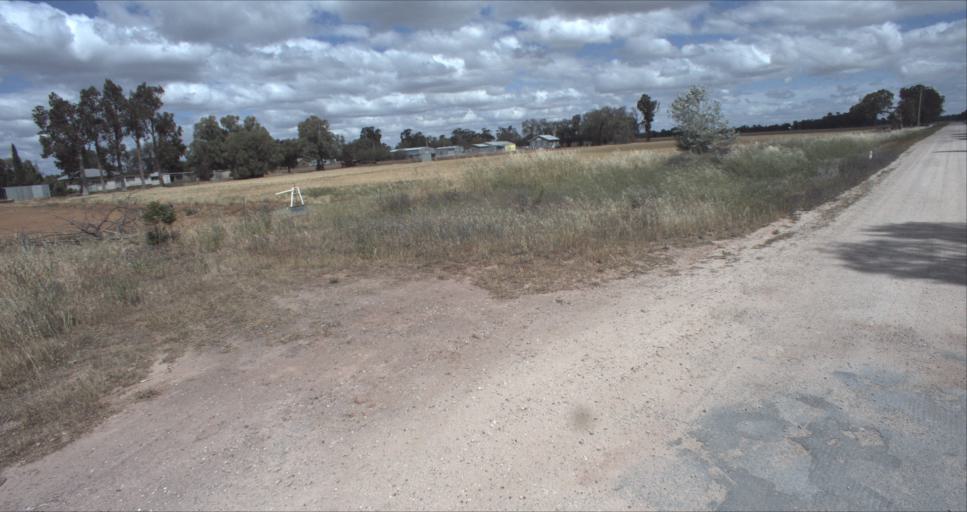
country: AU
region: New South Wales
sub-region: Leeton
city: Leeton
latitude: -34.5887
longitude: 146.3610
